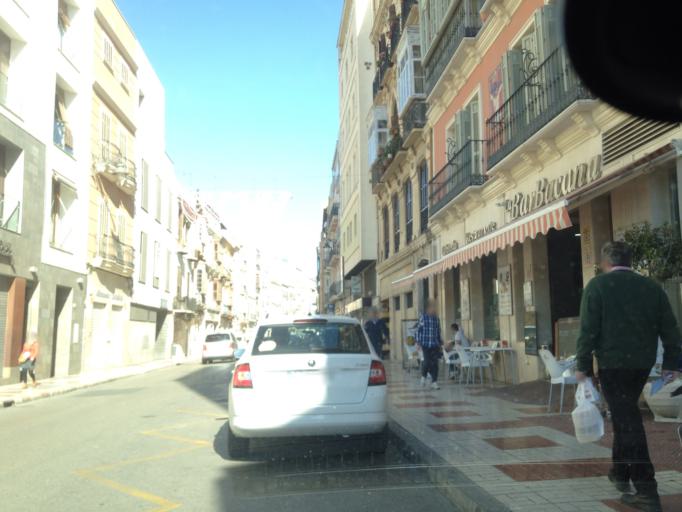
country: ES
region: Andalusia
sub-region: Provincia de Malaga
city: Malaga
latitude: 36.7217
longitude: -4.4250
